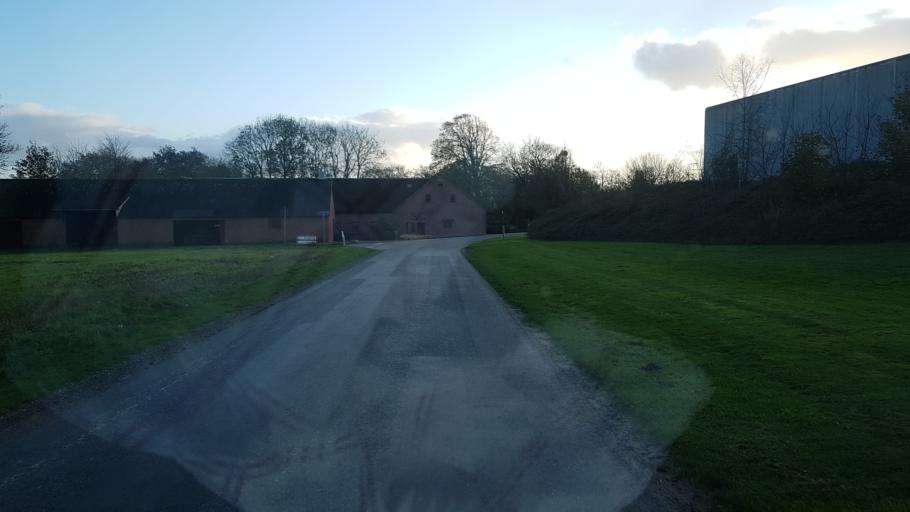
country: DK
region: South Denmark
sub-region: Vejen Kommune
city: Holsted
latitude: 55.4527
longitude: 8.9421
